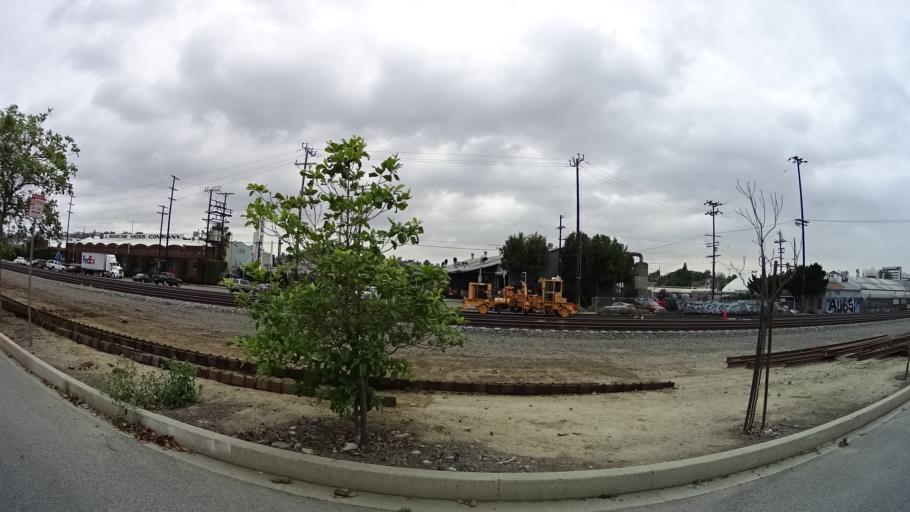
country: US
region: California
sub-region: Los Angeles County
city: Boyle Heights
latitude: 34.0636
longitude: -118.1934
